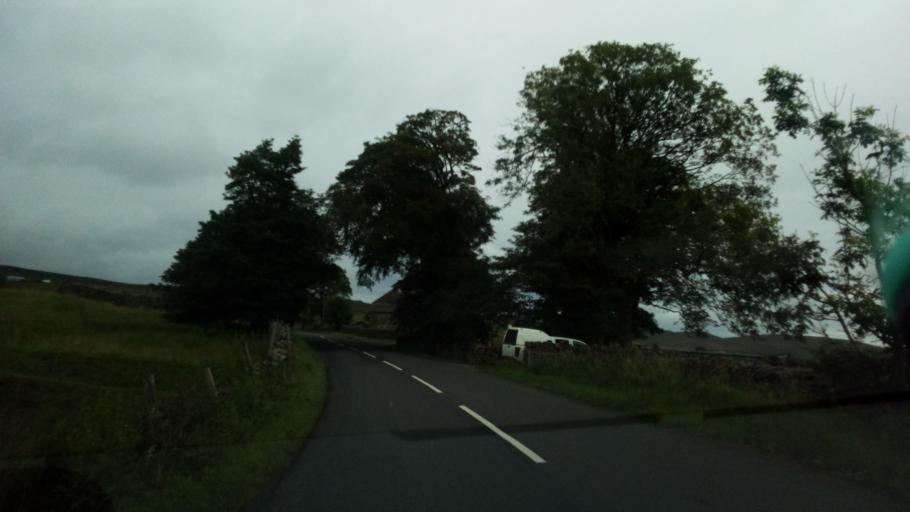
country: GB
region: England
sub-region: Cumbria
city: Kirkby Stephen
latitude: 54.5407
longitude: -2.2880
